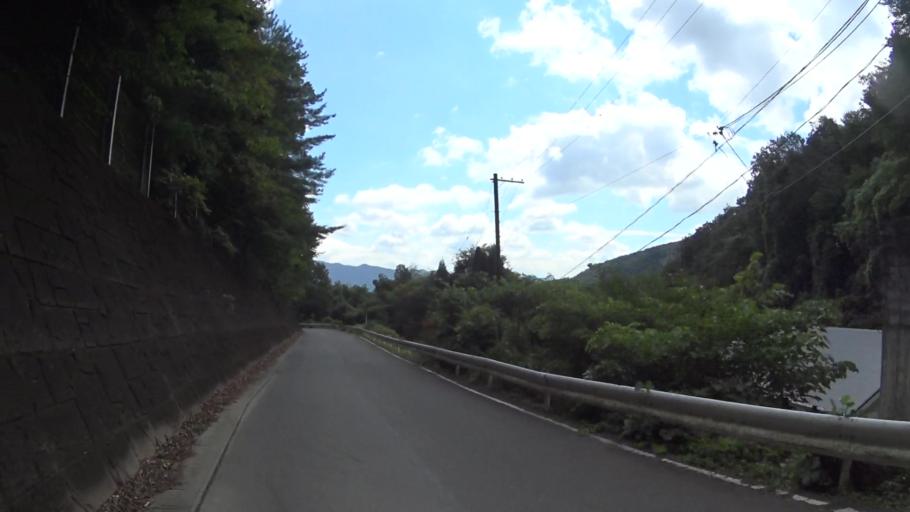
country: JP
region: Kyoto
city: Kyoto
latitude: 34.9793
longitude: 135.7888
